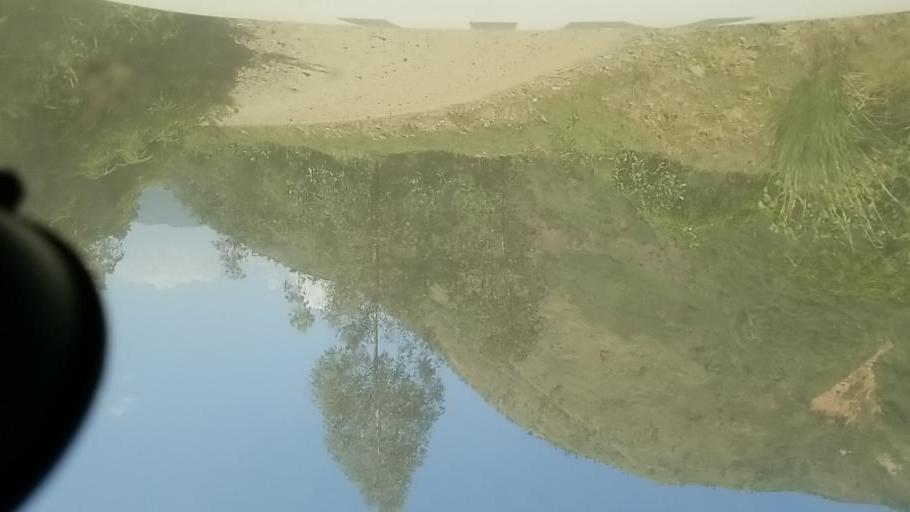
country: CD
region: Nord Kivu
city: Sake
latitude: -1.9663
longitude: 28.9149
